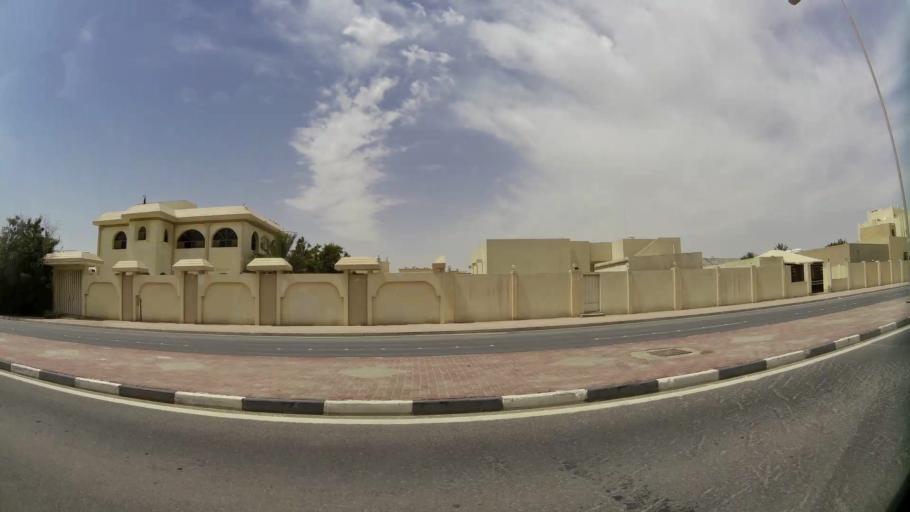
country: QA
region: Baladiyat ar Rayyan
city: Ar Rayyan
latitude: 25.2980
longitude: 51.4121
